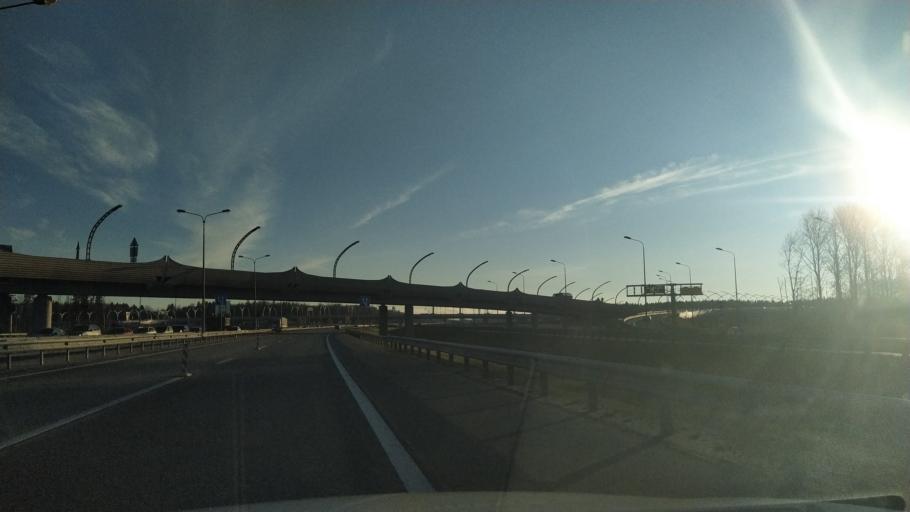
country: RU
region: St.-Petersburg
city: Pesochnyy
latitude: 60.0608
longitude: 30.1536
